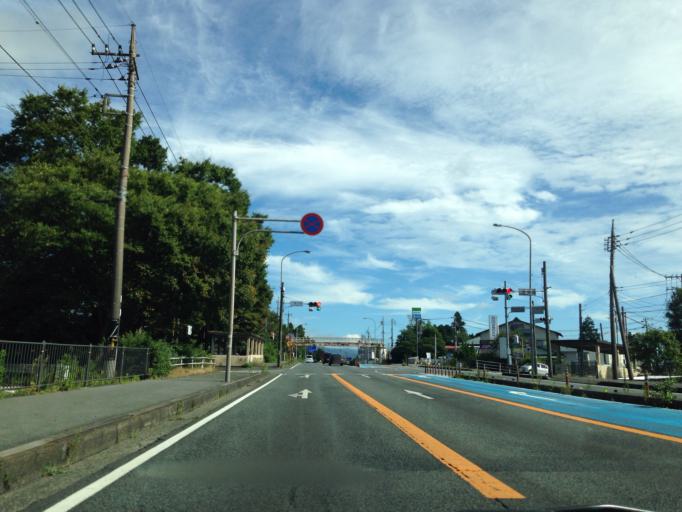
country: JP
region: Shizuoka
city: Gotemba
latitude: 35.2945
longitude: 138.9200
